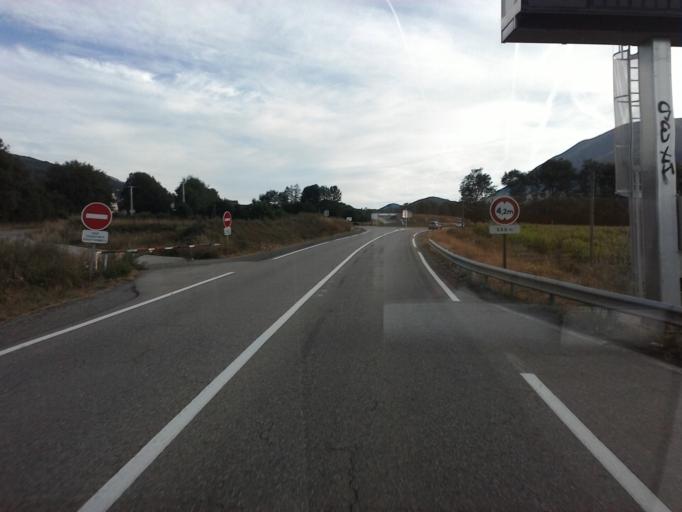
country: FR
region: Rhone-Alpes
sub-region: Departement de l'Isere
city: Pierre-Chatel
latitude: 44.9475
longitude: 5.7796
